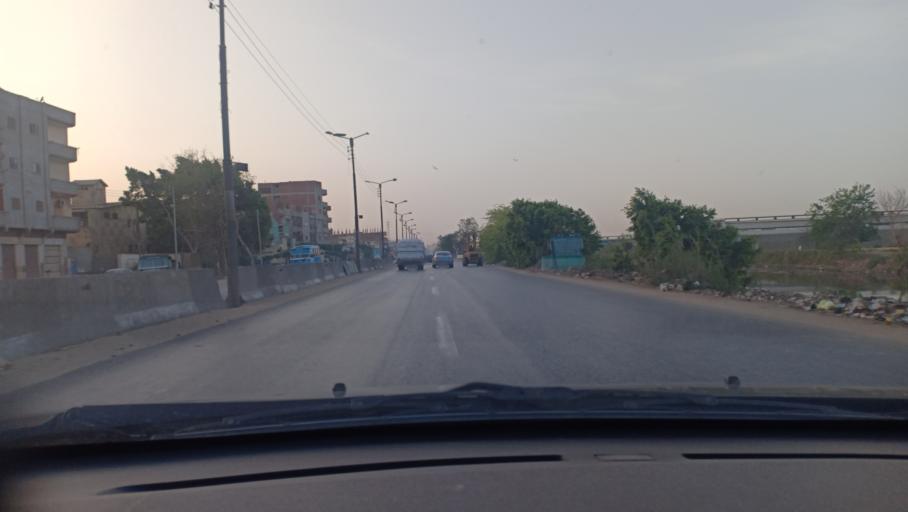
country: EG
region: Muhafazat al Gharbiyah
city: Zifta
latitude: 30.6852
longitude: 31.2804
